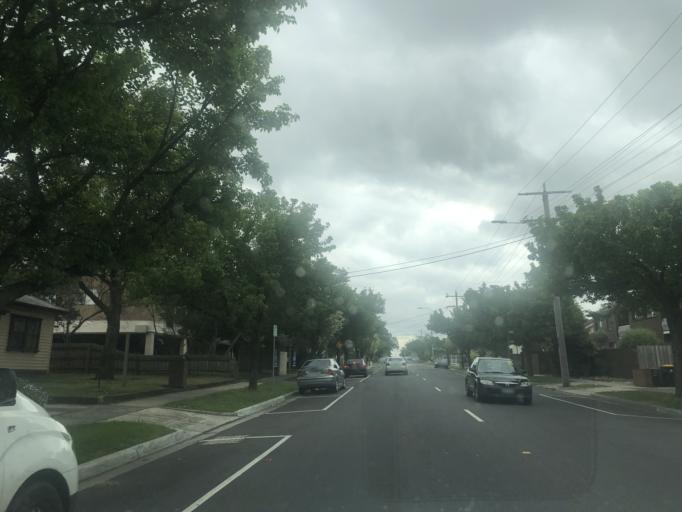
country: AU
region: Victoria
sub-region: Greater Dandenong
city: Dandenong
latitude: -37.9820
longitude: 145.2151
